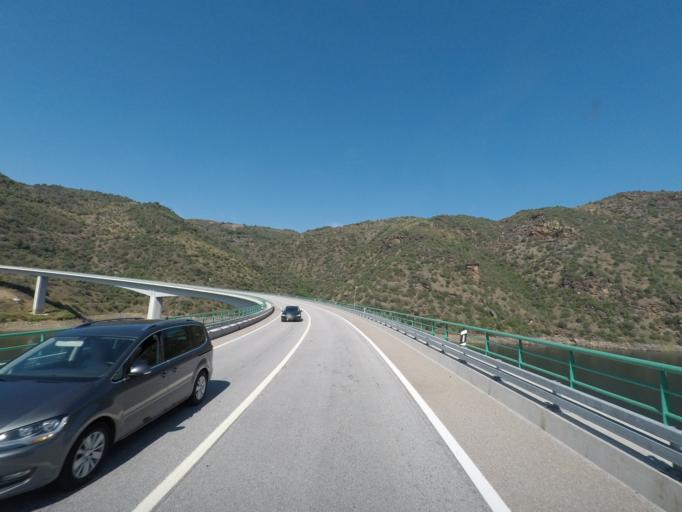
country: PT
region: Braganca
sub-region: Alfandega da Fe
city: Alfandega da Fe
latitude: 41.2867
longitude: -6.8722
